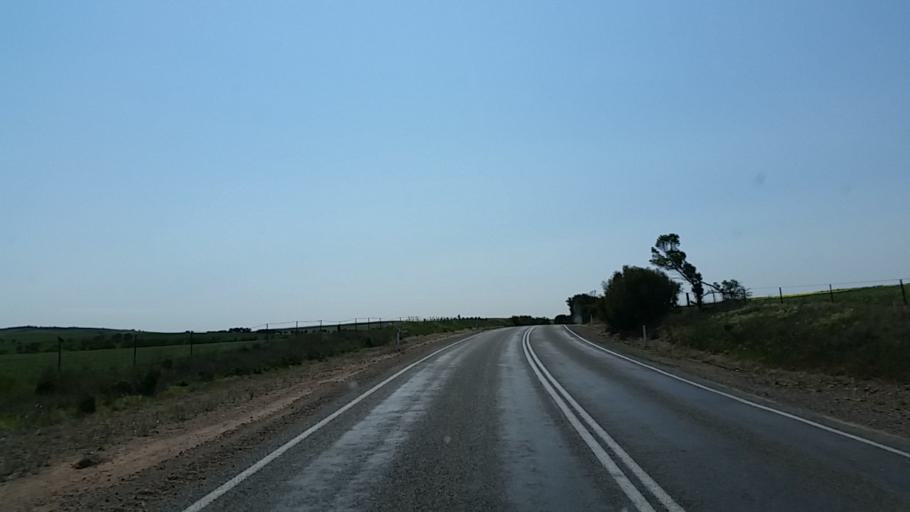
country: AU
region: South Australia
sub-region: Northern Areas
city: Jamestown
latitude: -33.2156
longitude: 138.4171
